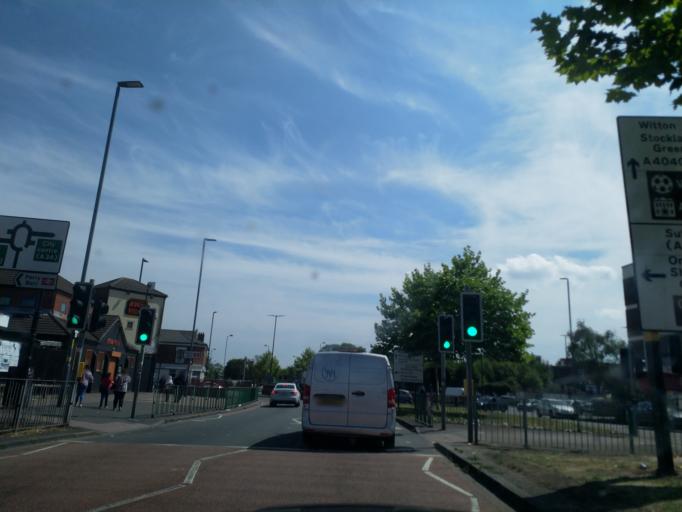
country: GB
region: England
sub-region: City and Borough of Birmingham
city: Hockley
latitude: 52.5155
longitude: -1.9027
